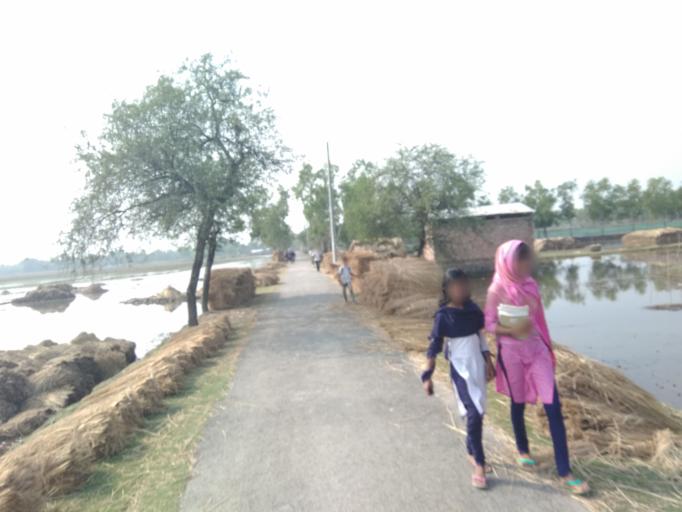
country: IN
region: West Bengal
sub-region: North 24 Parganas
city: Gosaba
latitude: 22.2611
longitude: 89.1153
